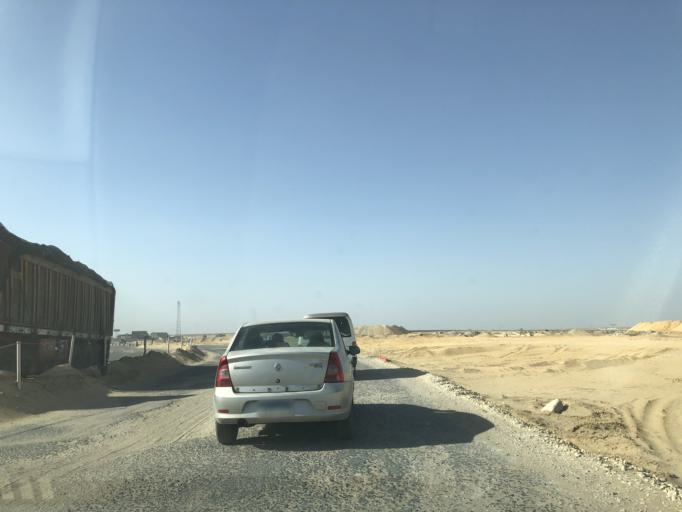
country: EG
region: Muhafazat al Minufiyah
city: Ashmun
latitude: 30.0615
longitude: 30.8471
